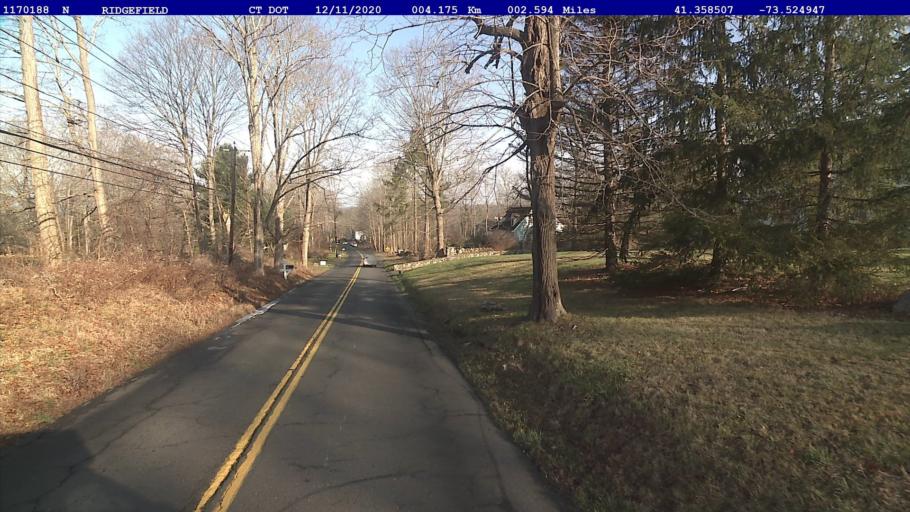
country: US
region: New York
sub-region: Putnam County
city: Peach Lake
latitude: 41.3585
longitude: -73.5249
